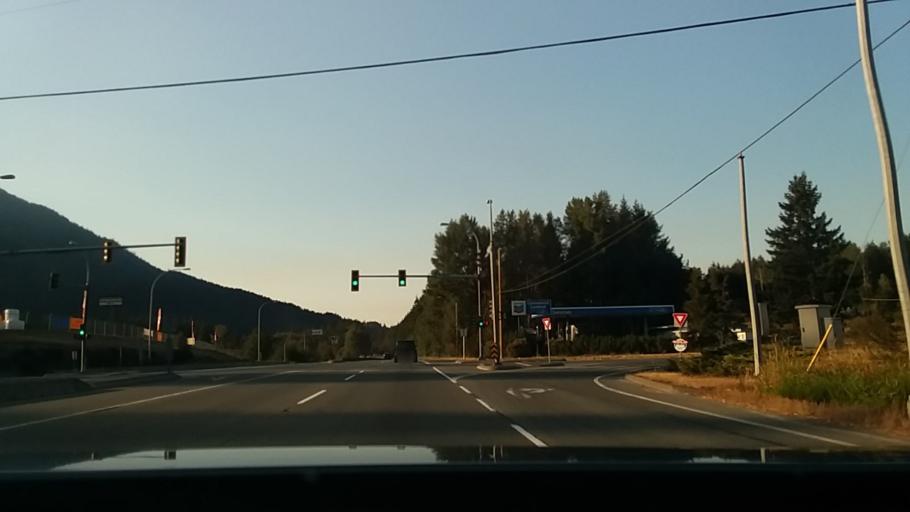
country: CA
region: British Columbia
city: North Cowichan
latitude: 48.8359
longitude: -123.7179
